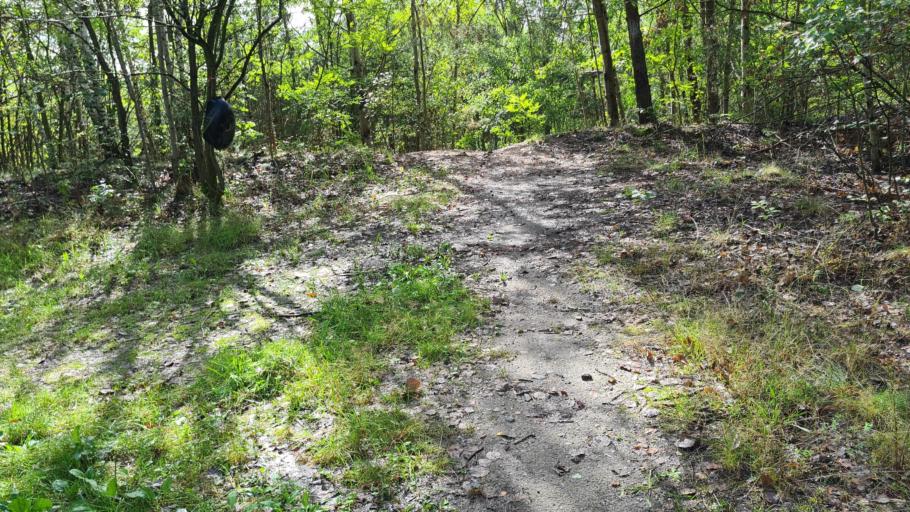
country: DE
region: Brandenburg
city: Sallgast
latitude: 51.5616
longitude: 13.8582
